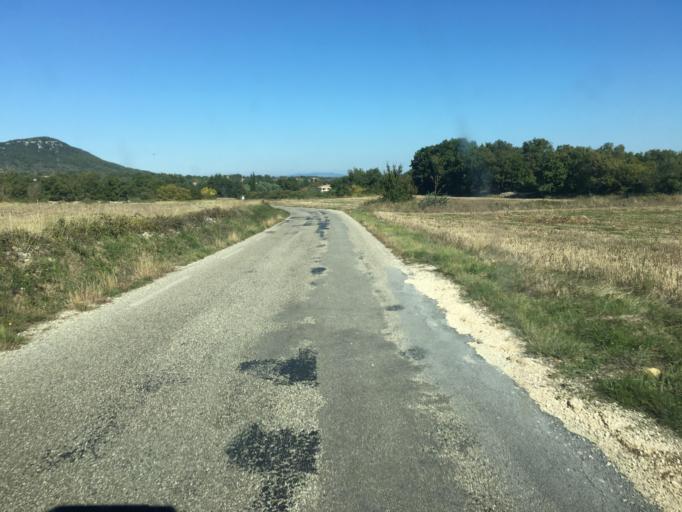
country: FR
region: Languedoc-Roussillon
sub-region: Departement du Gard
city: Barjac
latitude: 44.1786
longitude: 4.3258
